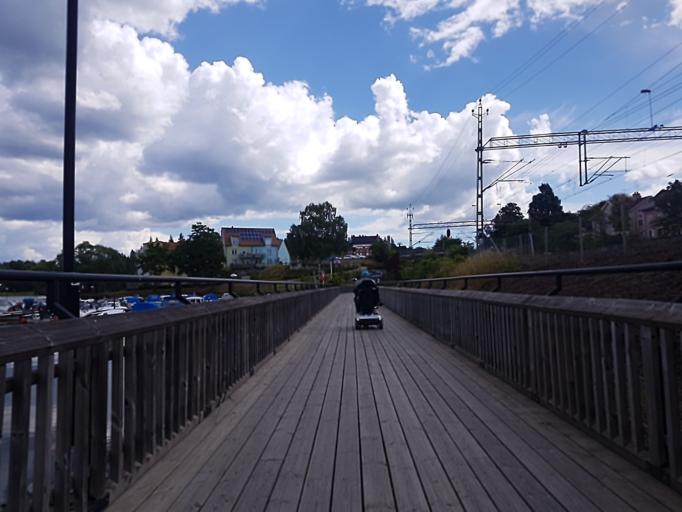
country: SE
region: Soedermanland
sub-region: Gnesta Kommun
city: Gnesta
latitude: 59.0486
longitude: 17.3145
